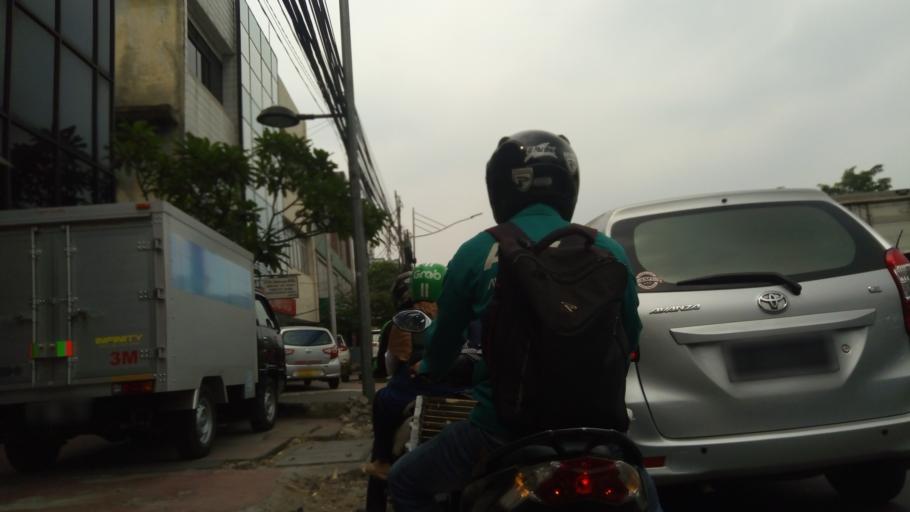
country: ID
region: Jakarta Raya
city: Jakarta
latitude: -6.1573
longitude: 106.8369
